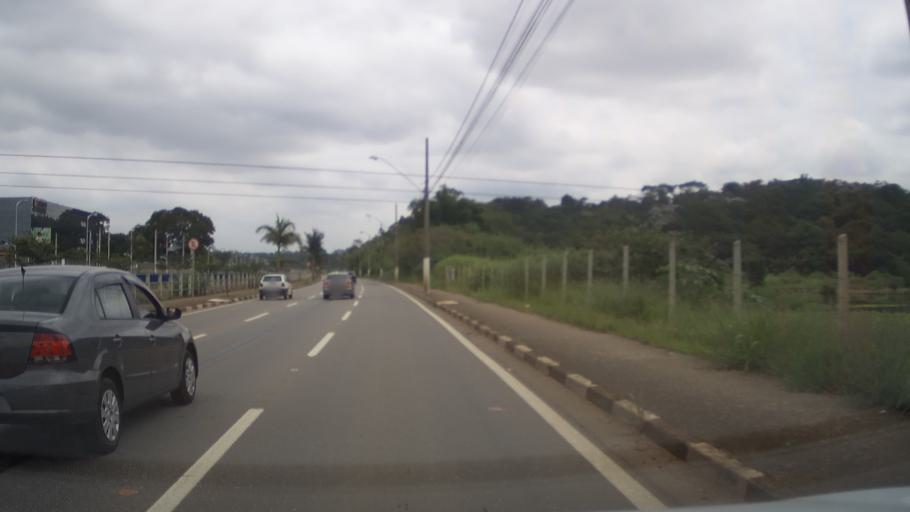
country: BR
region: Sao Paulo
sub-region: Aruja
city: Aruja
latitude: -23.4008
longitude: -46.3583
